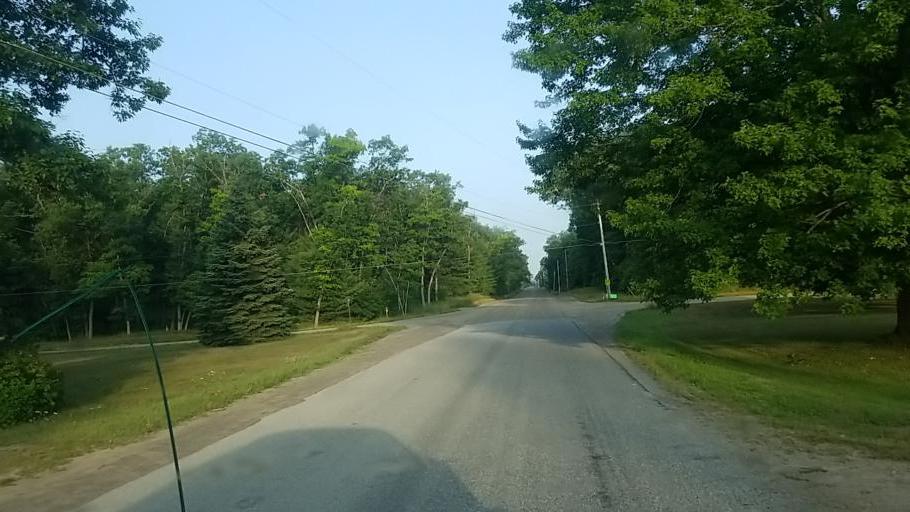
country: US
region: Michigan
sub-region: Muskegon County
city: Twin Lake
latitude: 43.4392
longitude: -86.0985
